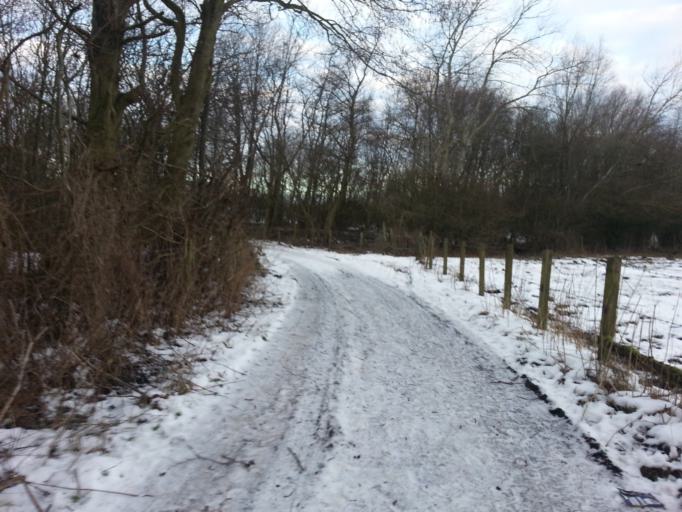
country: GB
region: England
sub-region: County Durham
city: Crook
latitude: 54.7241
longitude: -1.7526
